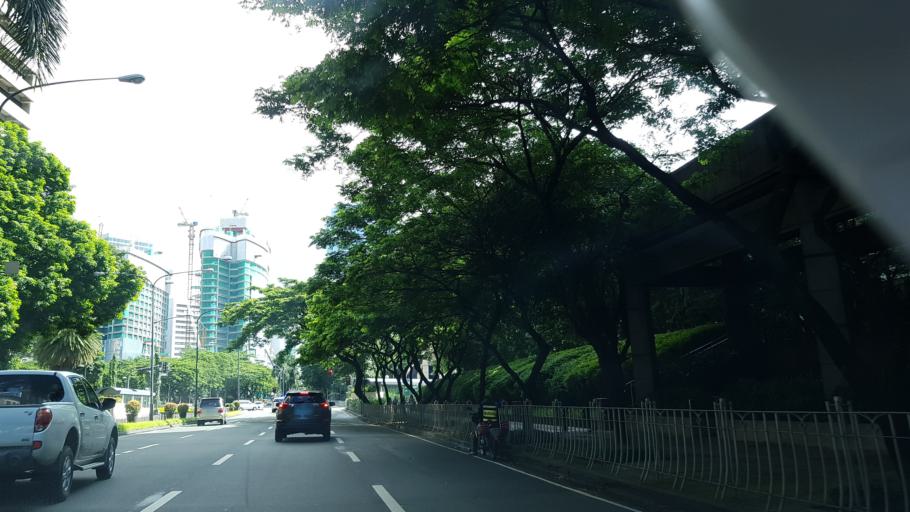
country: PH
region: Metro Manila
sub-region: Makati City
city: Makati City
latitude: 14.5534
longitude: 121.0241
